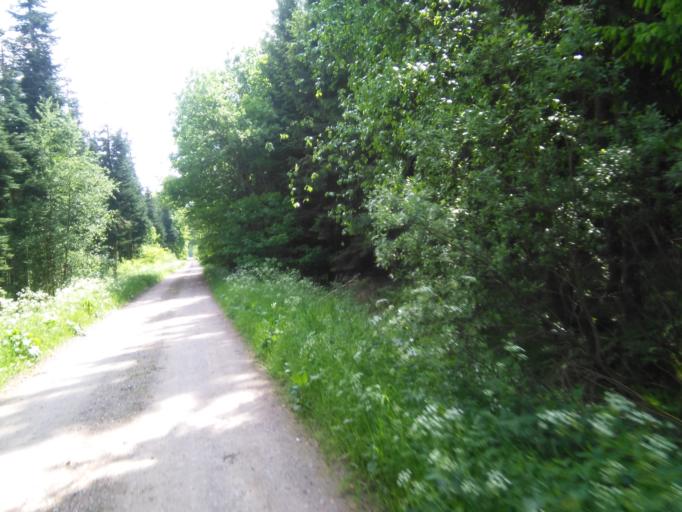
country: DK
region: Central Jutland
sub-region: Favrskov Kommune
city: Hinnerup
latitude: 56.2754
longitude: 10.0023
